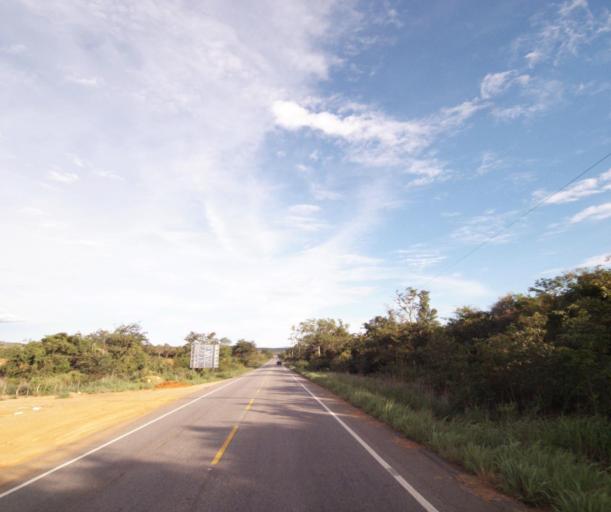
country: BR
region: Bahia
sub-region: Caetite
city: Caetite
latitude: -14.1221
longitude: -42.4238
